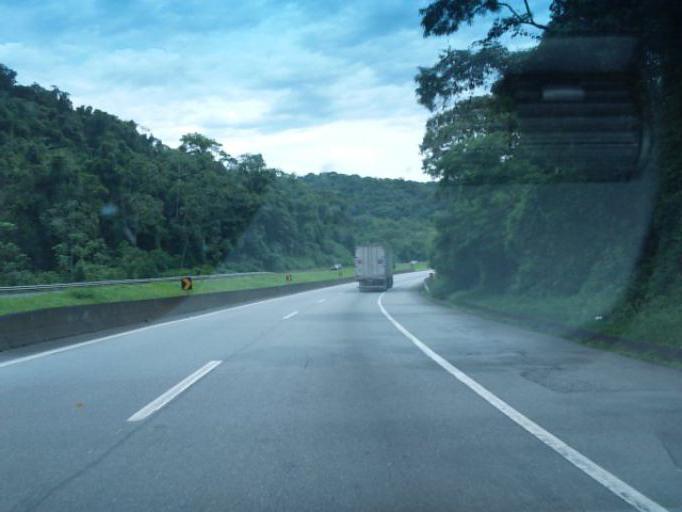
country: BR
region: Sao Paulo
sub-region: Miracatu
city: Miracatu
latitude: -24.1924
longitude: -47.3601
